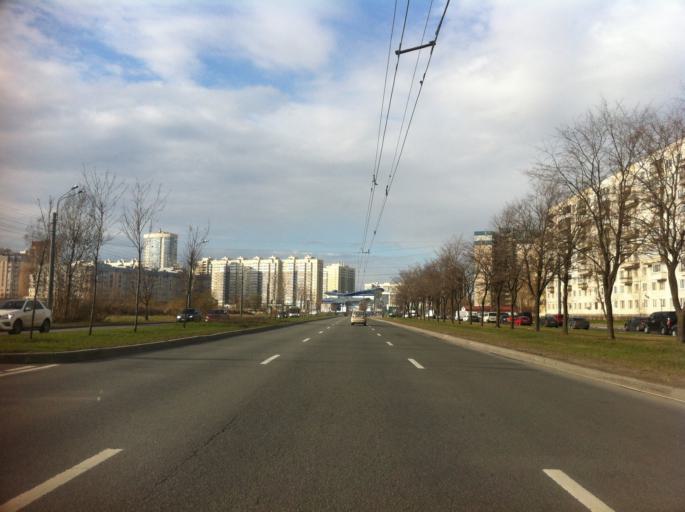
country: RU
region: St.-Petersburg
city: Uritsk
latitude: 59.8543
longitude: 30.1761
